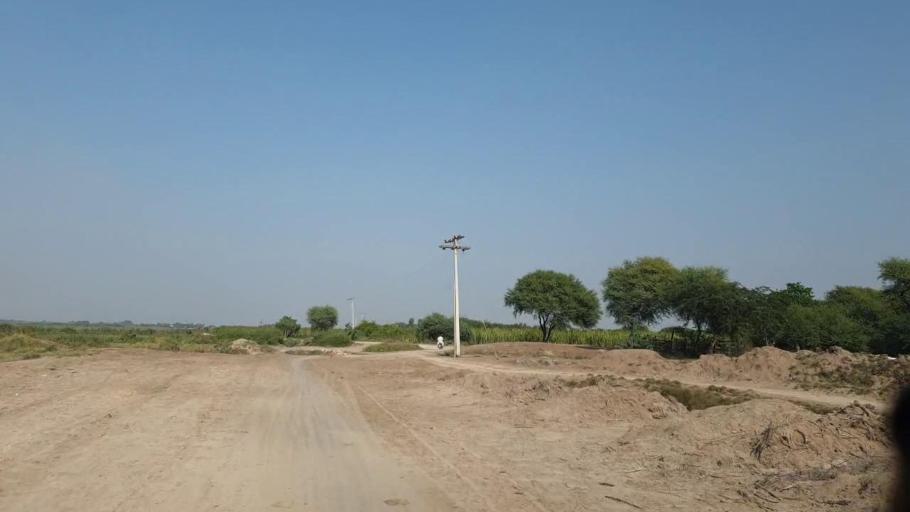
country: PK
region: Sindh
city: Bulri
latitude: 24.9312
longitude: 68.3814
